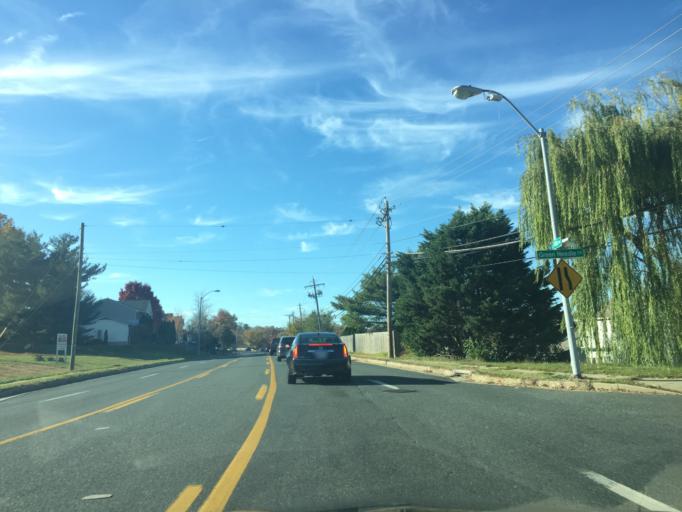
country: US
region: Maryland
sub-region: Baltimore County
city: Overlea
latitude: 39.3787
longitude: -76.5161
